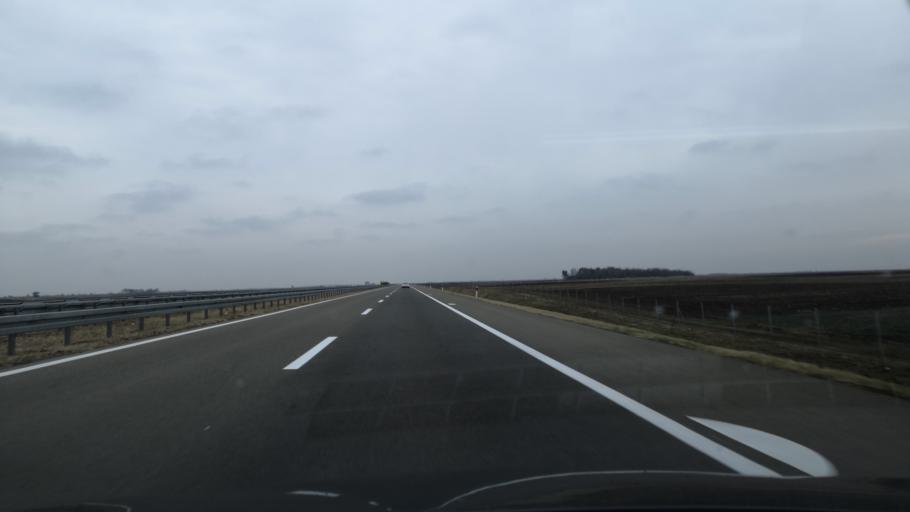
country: RS
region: Autonomna Pokrajina Vojvodina
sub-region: Severnobacki Okrug
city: Backa Topola
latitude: 45.8451
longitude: 19.6934
